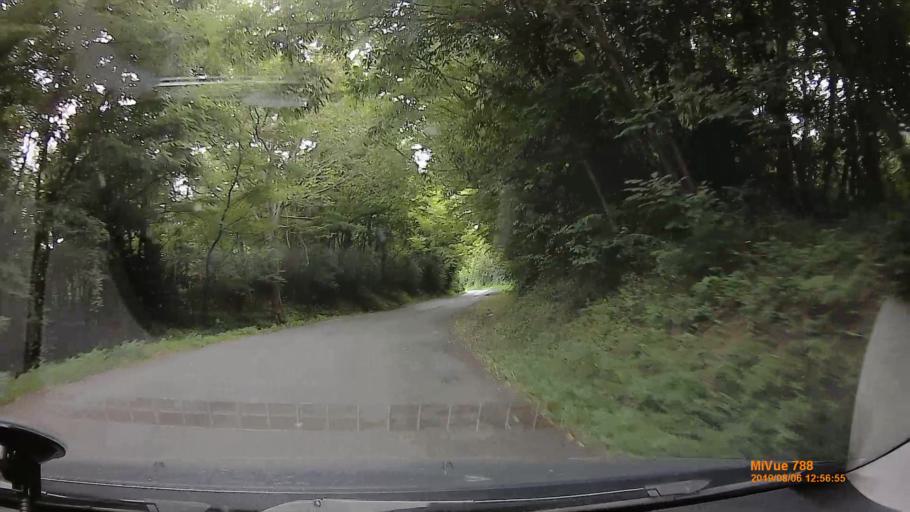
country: HU
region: Zala
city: Pacsa
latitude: 46.6349
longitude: 17.0347
